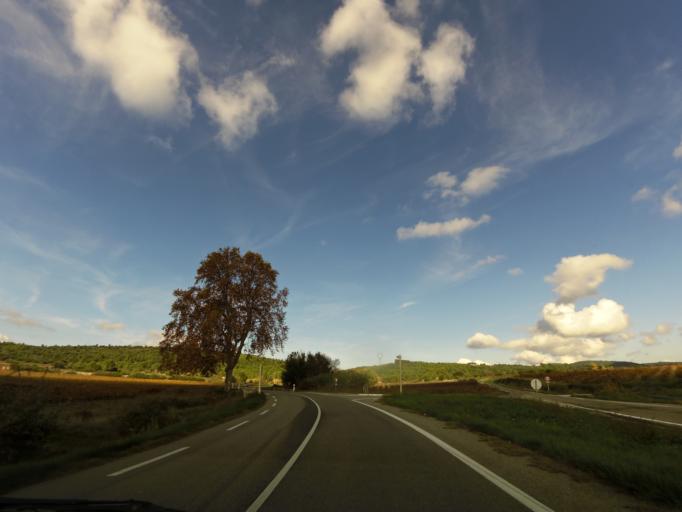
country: FR
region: Languedoc-Roussillon
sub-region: Departement du Gard
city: Villevieille
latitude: 43.8391
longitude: 4.0994
